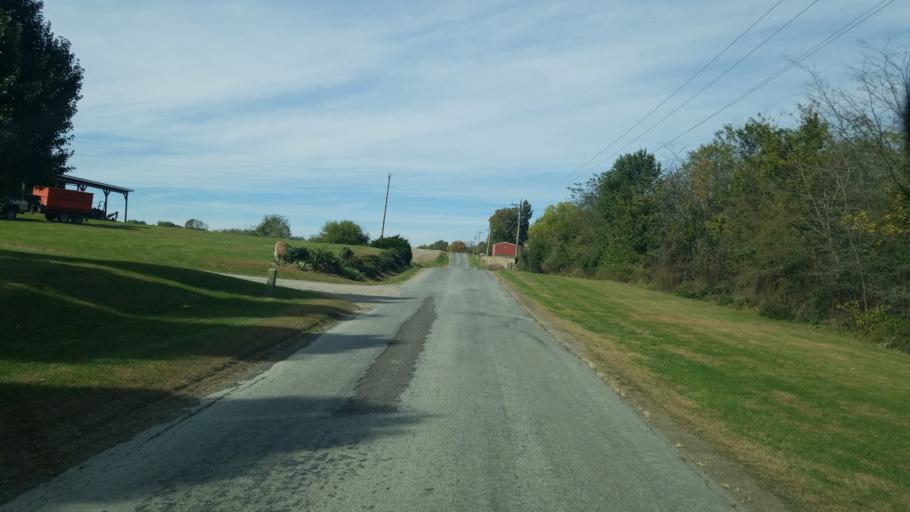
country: US
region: Ohio
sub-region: Highland County
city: Leesburg
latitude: 39.3158
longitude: -83.4677
